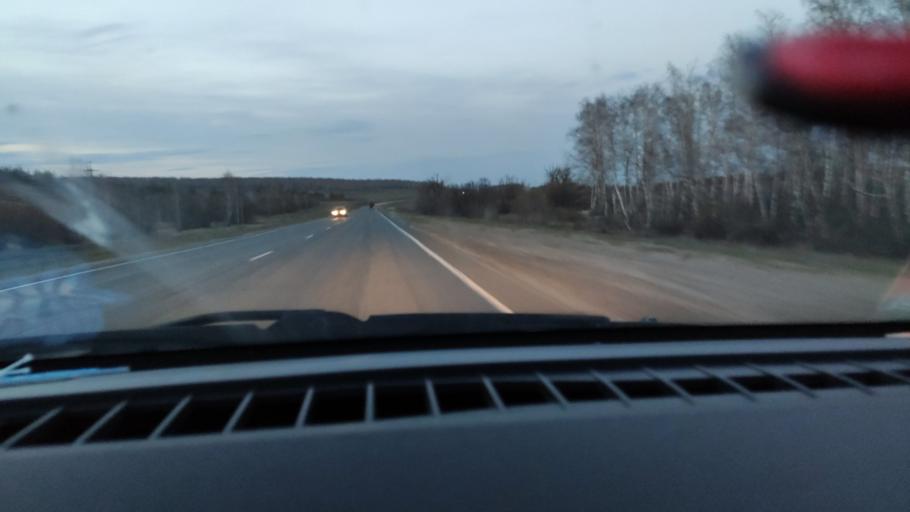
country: RU
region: Saratov
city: Sinodskoye
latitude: 52.0652
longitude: 46.7684
